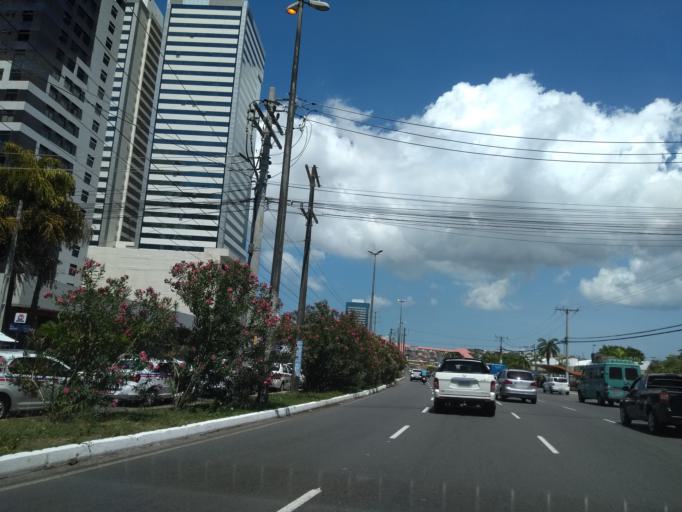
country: BR
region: Bahia
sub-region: Salvador
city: Salvador
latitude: -12.9796
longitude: -38.4506
